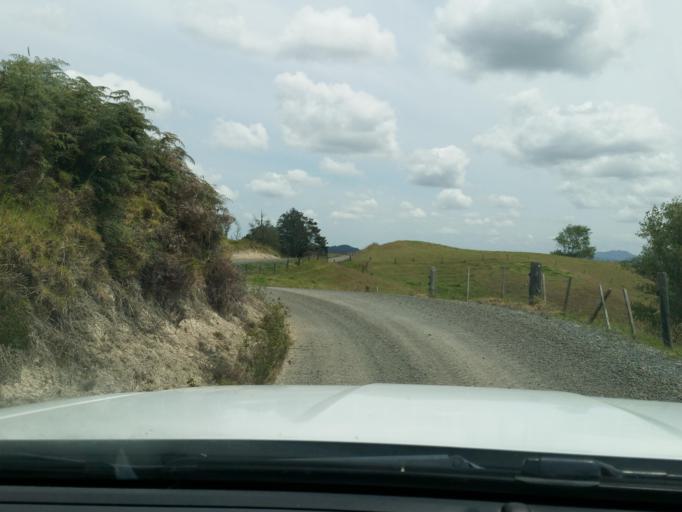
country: NZ
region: Northland
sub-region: Whangarei
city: Maungatapere
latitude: -35.9828
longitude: 174.2226
